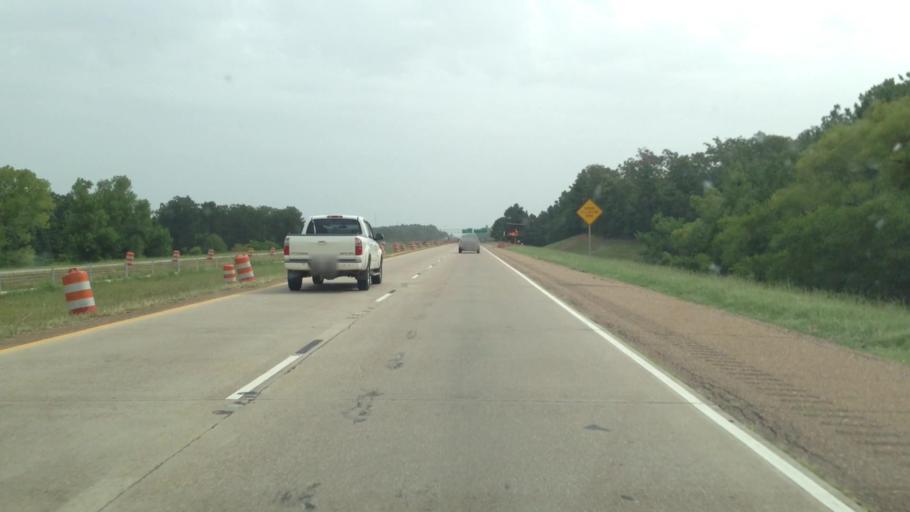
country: US
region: Louisiana
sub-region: Caddo Parish
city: Shreveport
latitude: 32.4665
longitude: -93.8421
